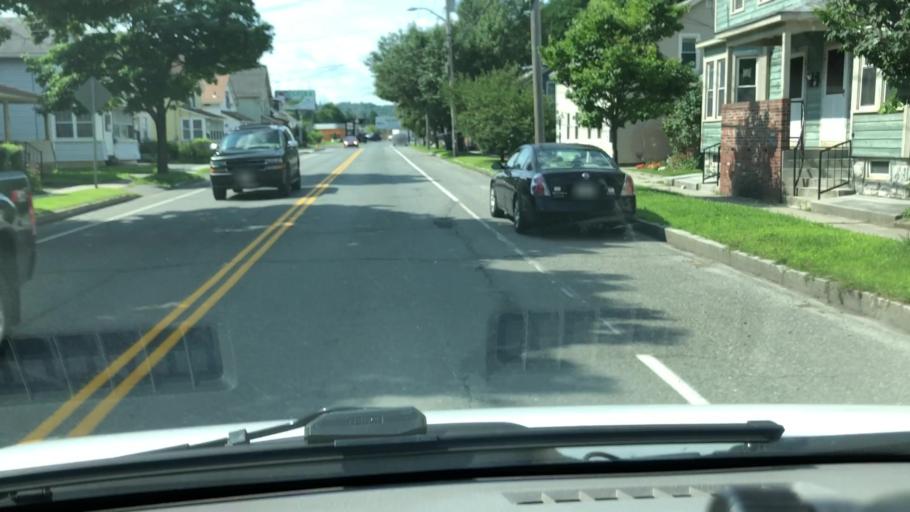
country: US
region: Massachusetts
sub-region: Berkshire County
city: Adams
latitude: 42.6320
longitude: -73.1145
